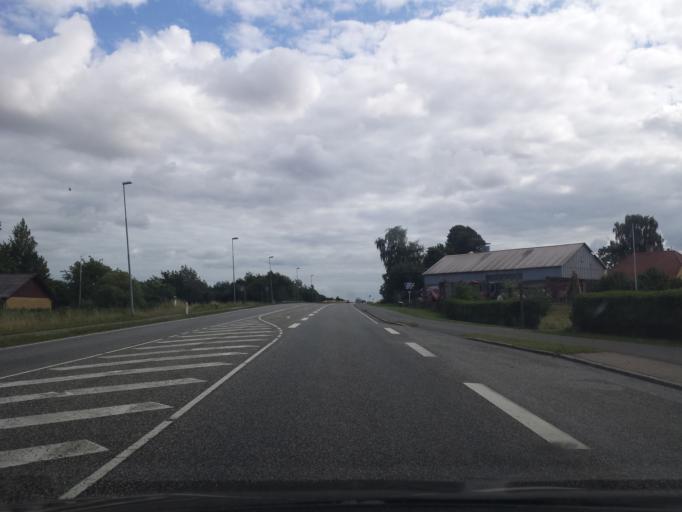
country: DK
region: South Denmark
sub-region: Sonderborg Kommune
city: Augustenborg
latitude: 54.9653
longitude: 9.8993
